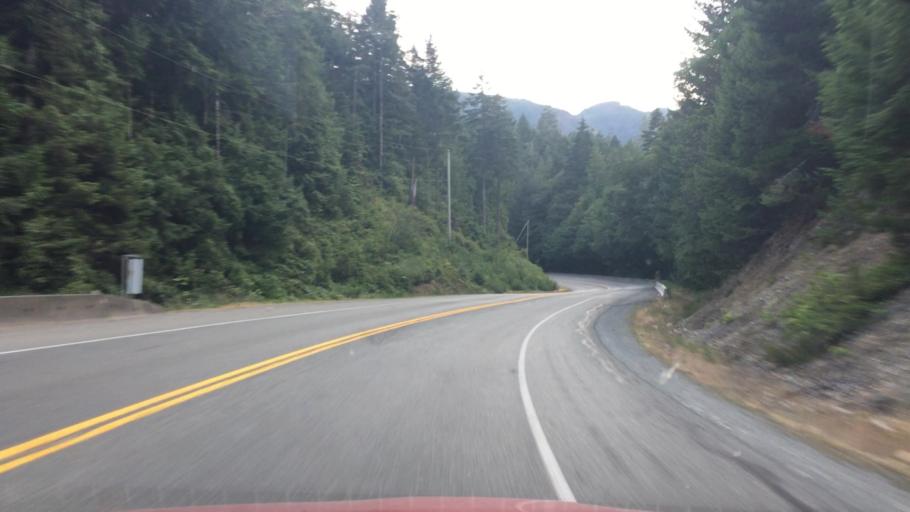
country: CA
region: British Columbia
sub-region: Regional District of Nanaimo
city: Parksville
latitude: 49.3013
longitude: -124.5561
